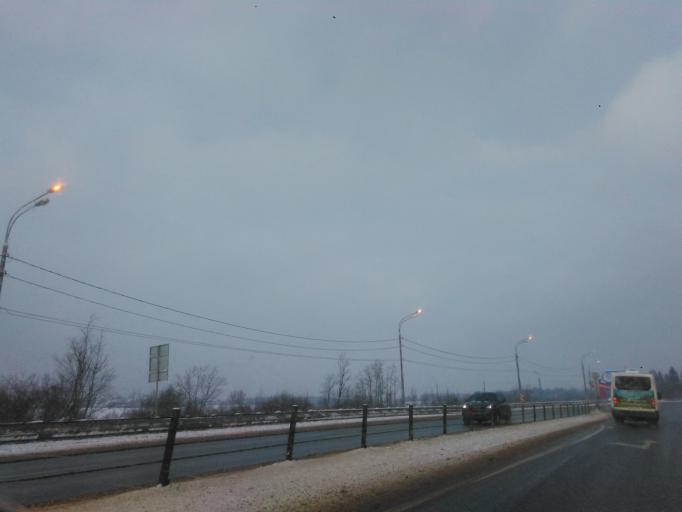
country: RU
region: Moskovskaya
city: Dedenevo
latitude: 56.2171
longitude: 37.5216
